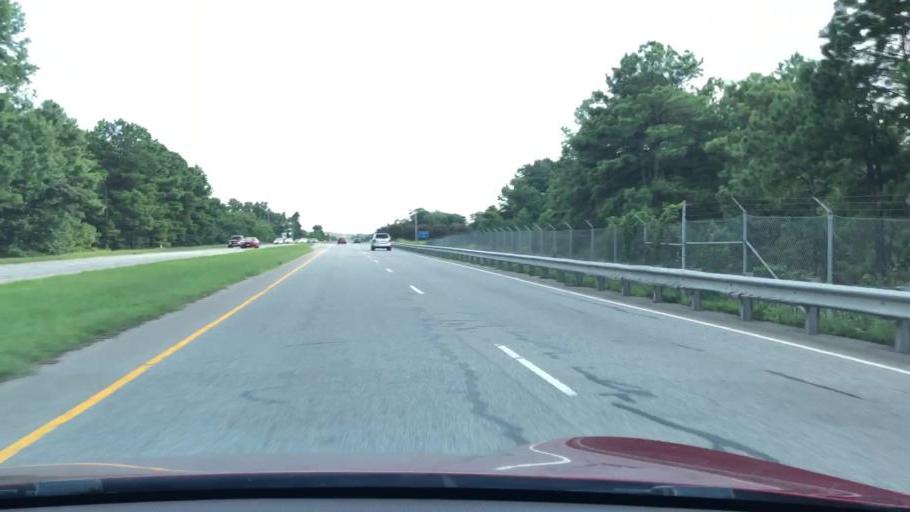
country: US
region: Virginia
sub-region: City of Virginia Beach
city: Virginia Beach
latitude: 36.8298
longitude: -76.0110
